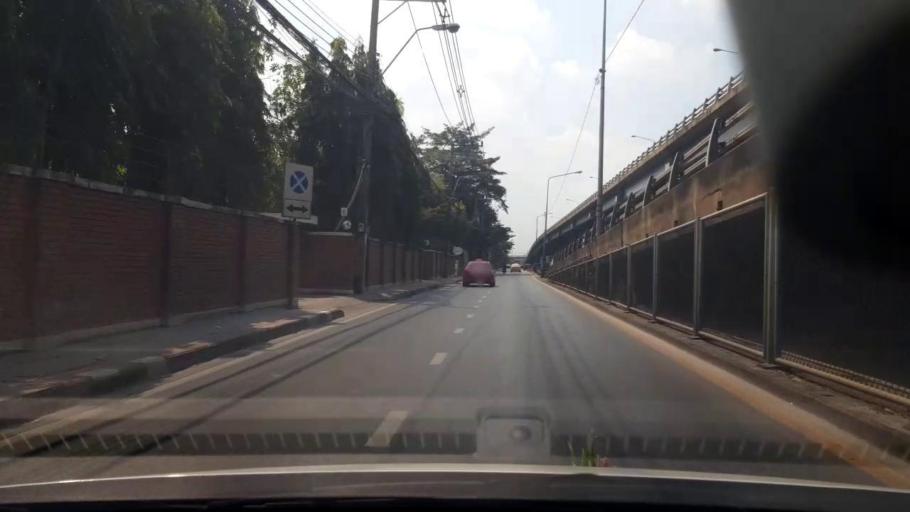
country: TH
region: Bangkok
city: Bang Sue
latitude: 13.8268
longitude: 100.5270
